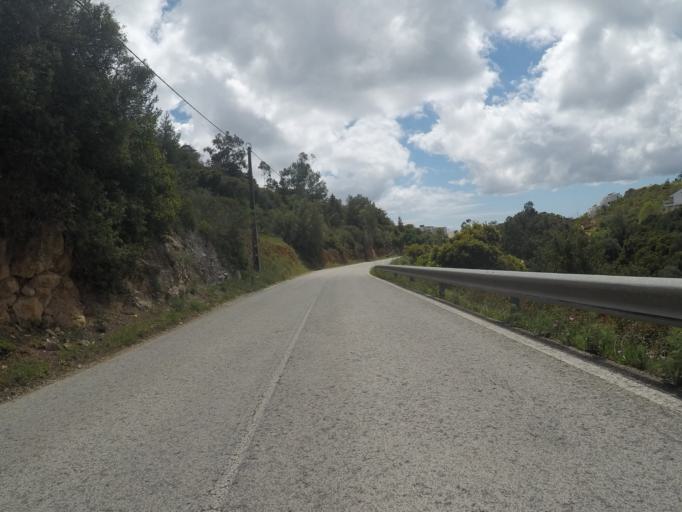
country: PT
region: Faro
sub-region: Vila do Bispo
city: Vila do Bispo
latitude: 37.0690
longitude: -8.8250
